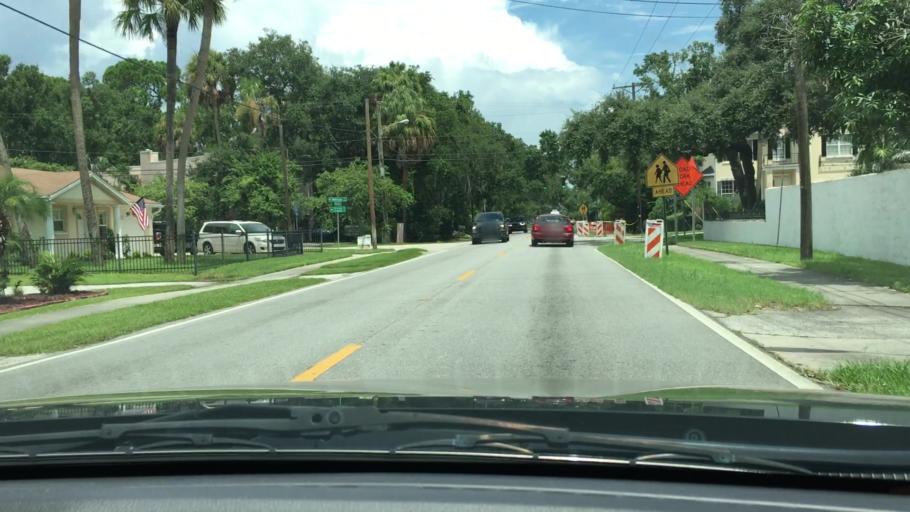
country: US
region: Florida
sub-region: Hillsborough County
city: Tampa
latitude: 27.9272
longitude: -82.5244
